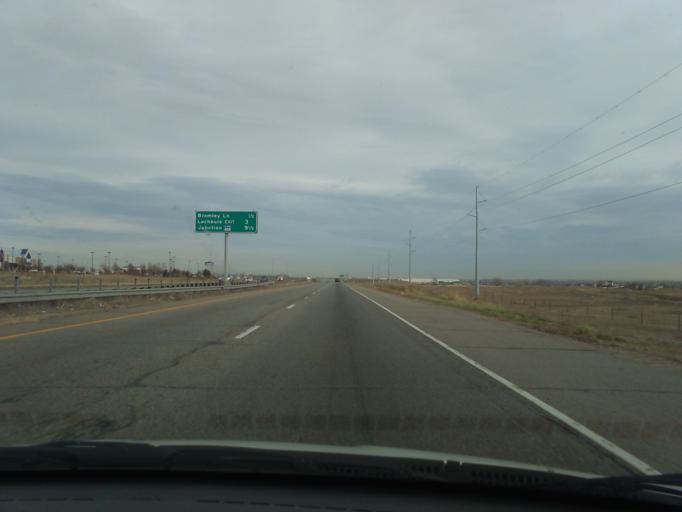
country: US
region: Colorado
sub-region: Weld County
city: Lochbuie
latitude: 39.9651
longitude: -104.7586
